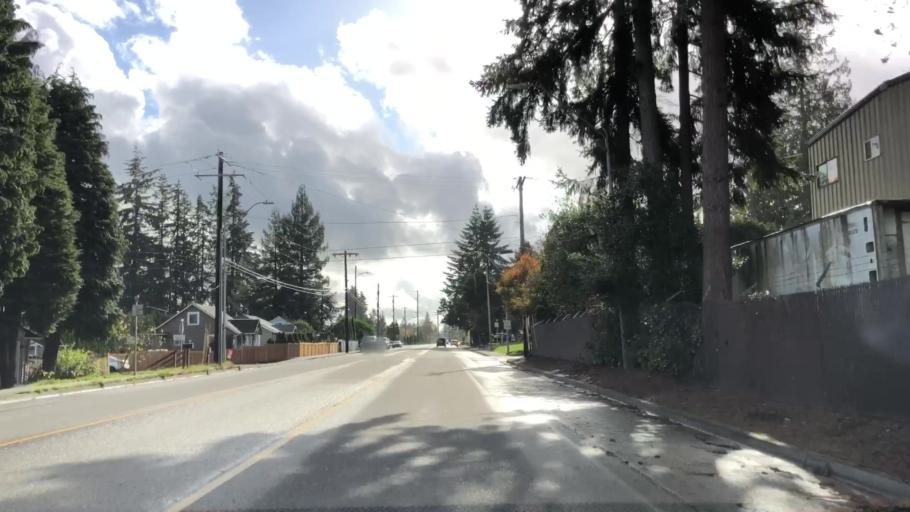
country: US
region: Washington
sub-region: Snohomish County
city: Everett
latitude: 47.9438
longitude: -122.2068
